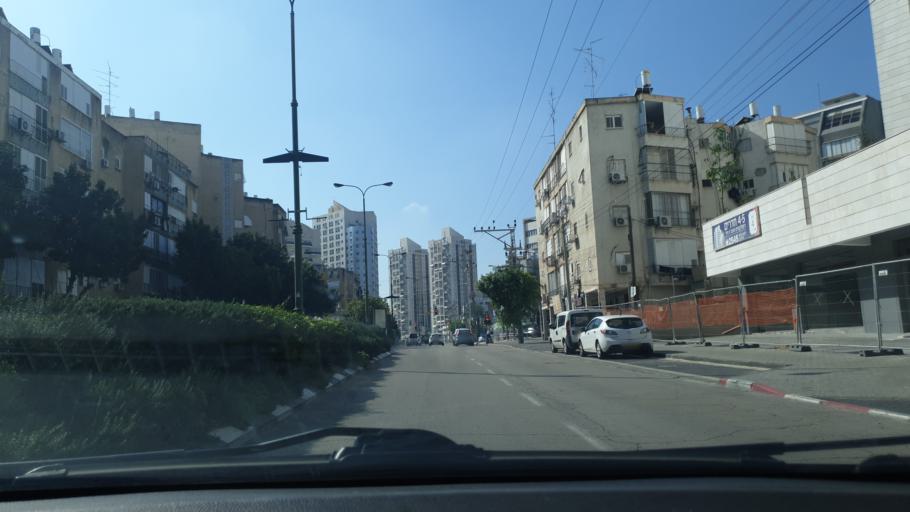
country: IL
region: Central District
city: Rishon LeZiyyon
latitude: 31.9700
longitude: 34.8051
